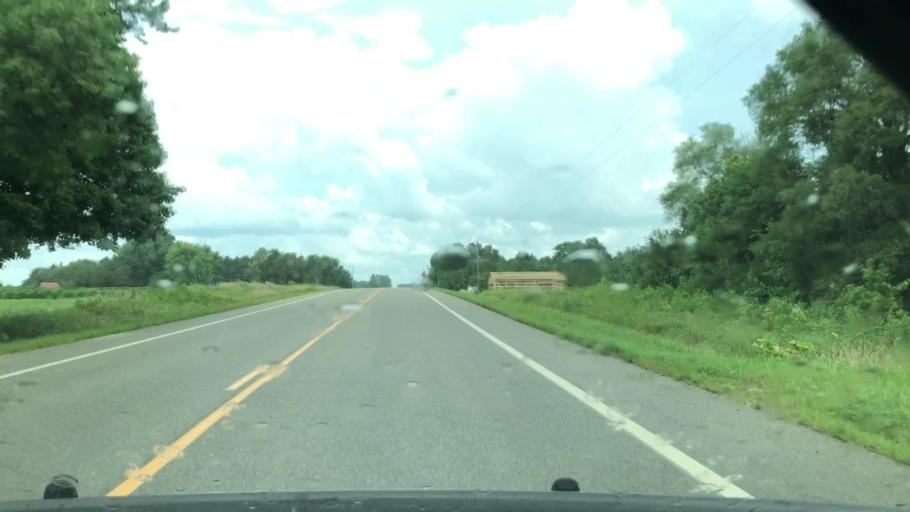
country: US
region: Minnesota
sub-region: Olmsted County
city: Stewartville
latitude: 43.8721
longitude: -92.5285
